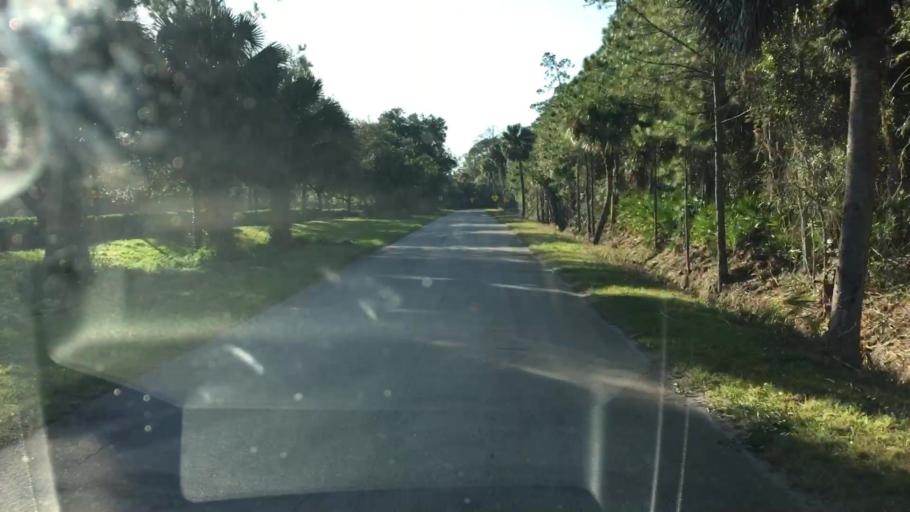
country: US
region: Florida
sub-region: Volusia County
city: Ormond-by-the-Sea
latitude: 29.3324
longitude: -81.1221
